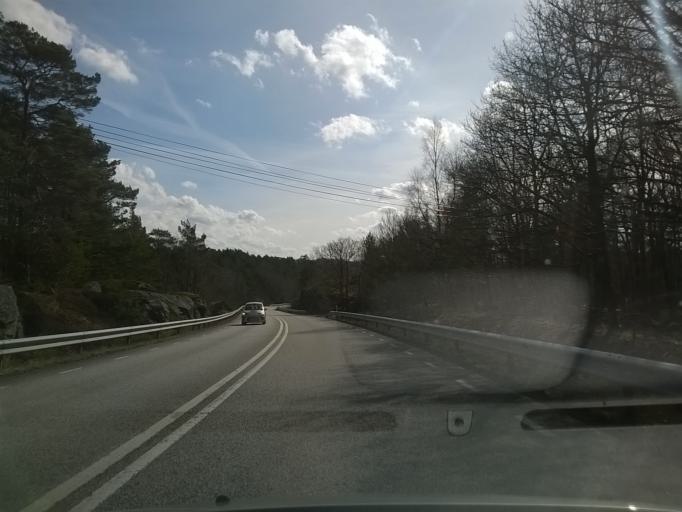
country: SE
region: Vaestra Goetaland
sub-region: Tjorns Kommun
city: Myggenas
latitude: 58.0805
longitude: 11.6950
